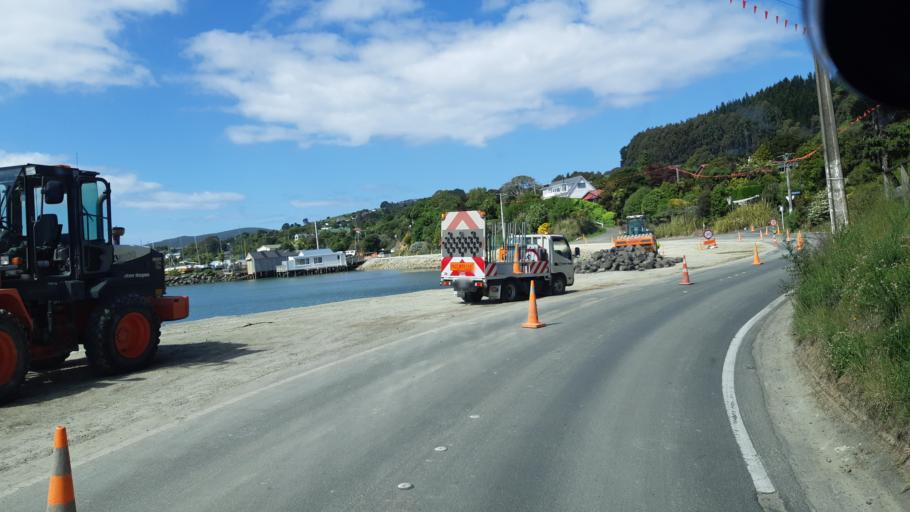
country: NZ
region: Otago
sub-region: Dunedin City
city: Portobello
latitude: -45.8487
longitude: 170.6179
